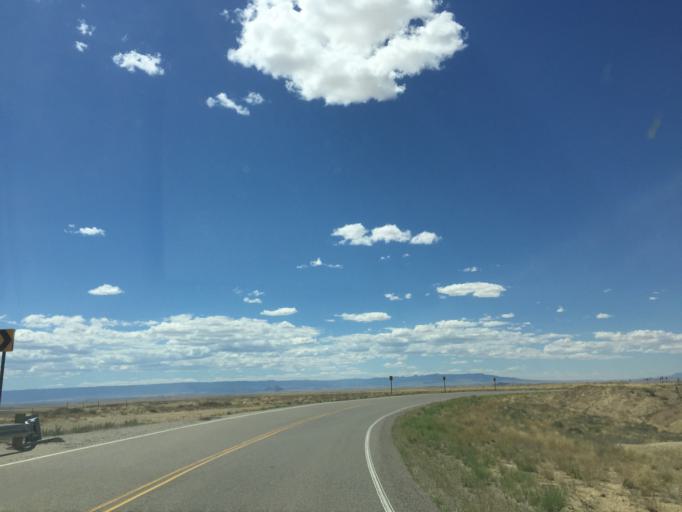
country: US
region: New Mexico
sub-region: San Juan County
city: Upper Fruitland
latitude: 36.4189
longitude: -108.4250
